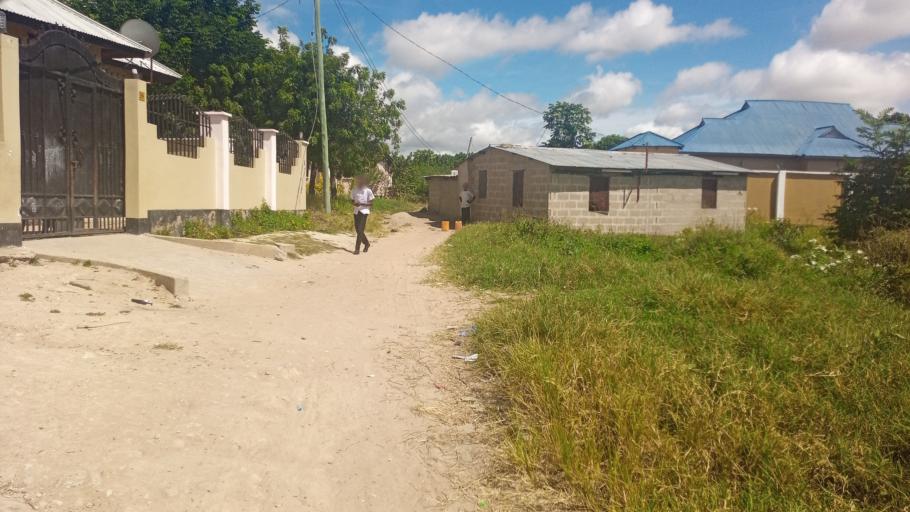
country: TZ
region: Dodoma
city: Dodoma
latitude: -6.1919
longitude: 35.7236
